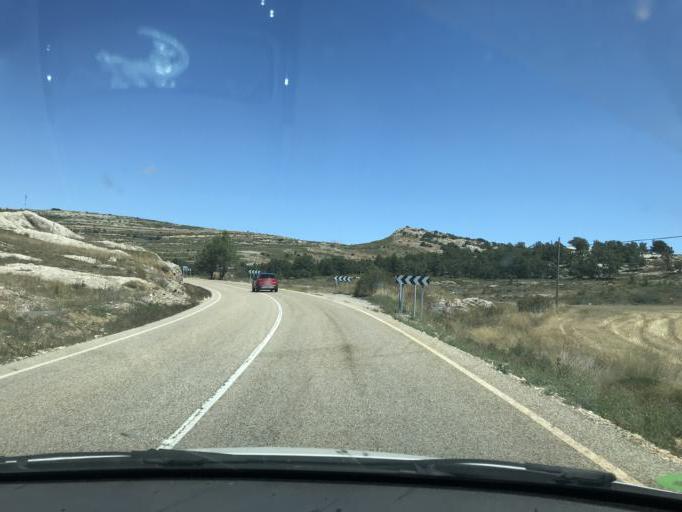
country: ES
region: Castille and Leon
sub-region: Provincia de Palencia
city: Dehesa de Montejo
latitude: 42.8144
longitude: -4.4443
